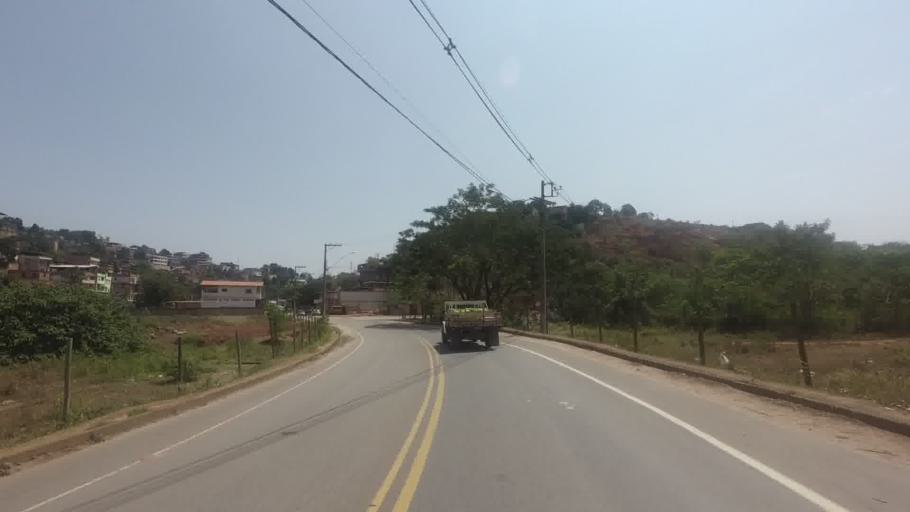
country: BR
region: Espirito Santo
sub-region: Cachoeiro De Itapemirim
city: Cachoeiro de Itapemirim
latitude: -20.8503
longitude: -41.0996
